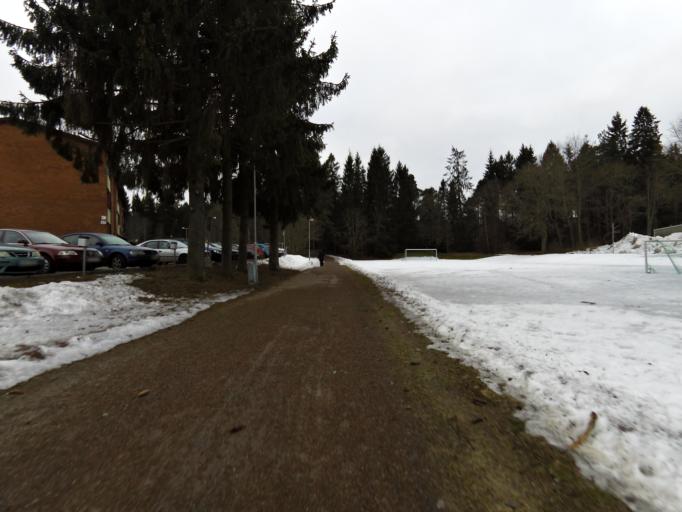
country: SE
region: Gaevleborg
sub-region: Gavle Kommun
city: Gavle
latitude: 60.6574
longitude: 17.1520
